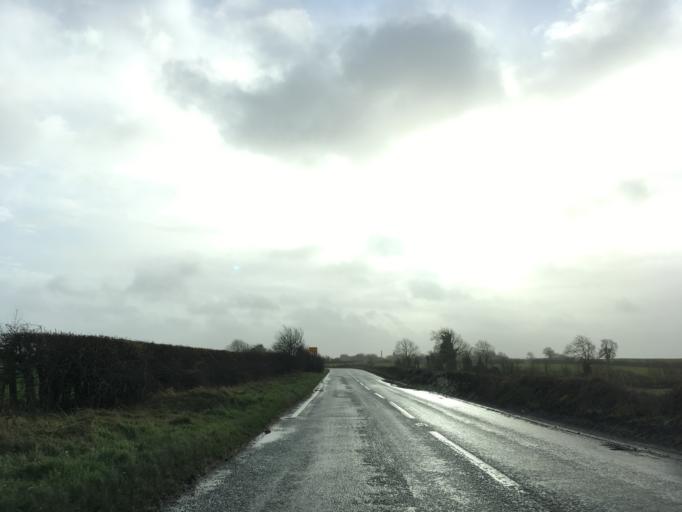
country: GB
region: England
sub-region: South Gloucestershire
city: Charfield
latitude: 51.6171
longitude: -2.4159
